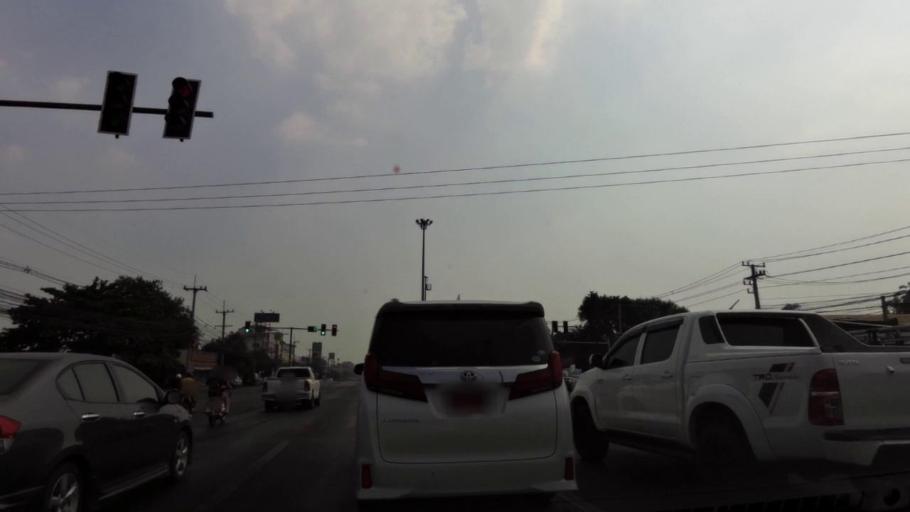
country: TH
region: Phra Nakhon Si Ayutthaya
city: Phra Nakhon Si Ayutthaya
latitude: 14.3534
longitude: 100.6000
